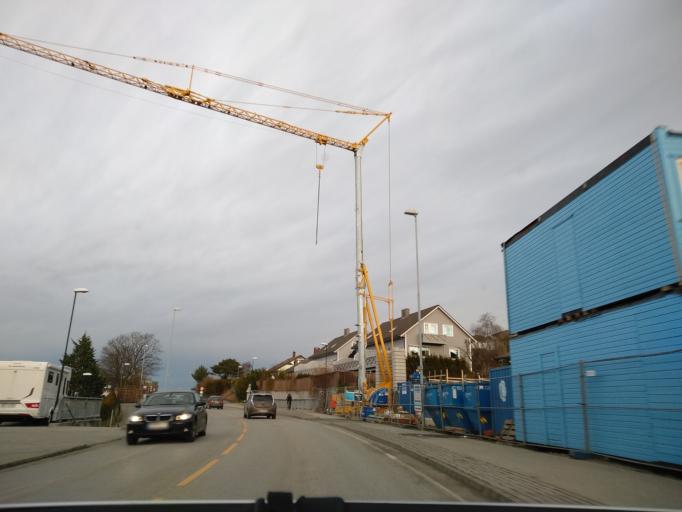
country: NO
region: Rogaland
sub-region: Stavanger
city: Stavanger
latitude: 58.9486
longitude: 5.6737
